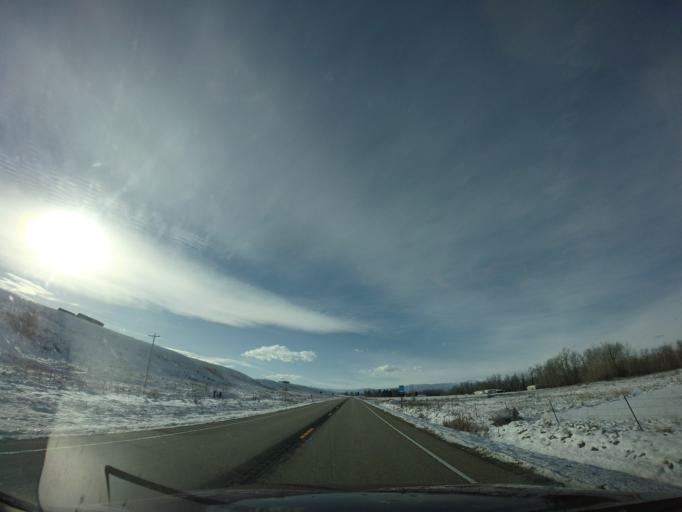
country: US
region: Montana
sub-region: Carbon County
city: Red Lodge
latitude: 45.3900
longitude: -109.1340
